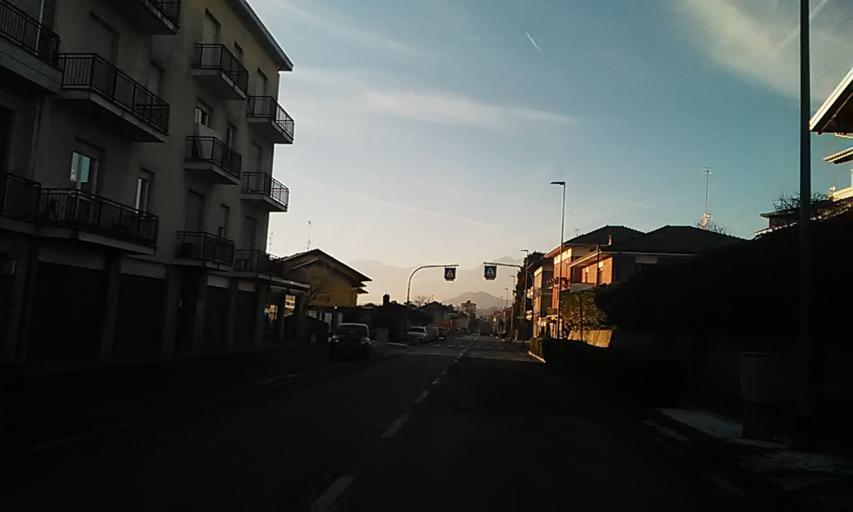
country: IT
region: Piedmont
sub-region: Provincia di Biella
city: Cossato
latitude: 45.5662
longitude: 8.1976
